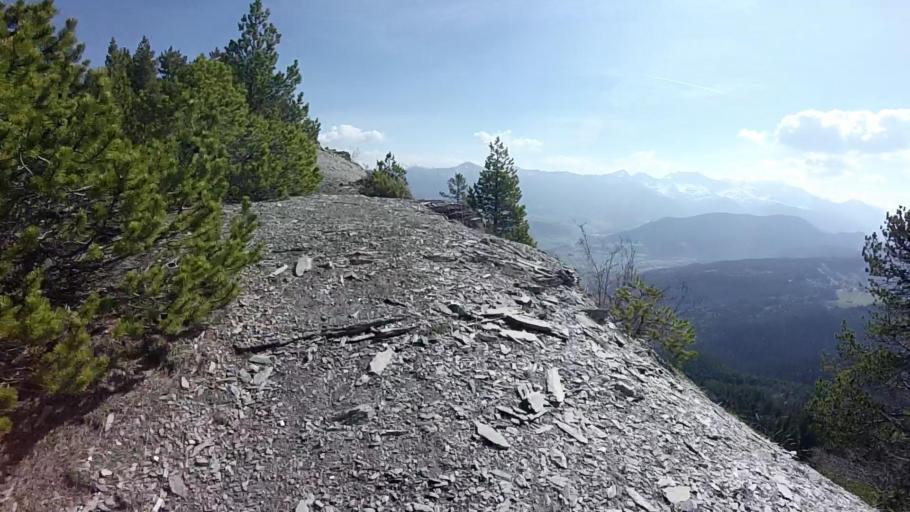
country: FR
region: Provence-Alpes-Cote d'Azur
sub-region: Departement des Alpes-de-Haute-Provence
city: Seyne-les-Alpes
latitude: 44.3394
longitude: 6.3012
